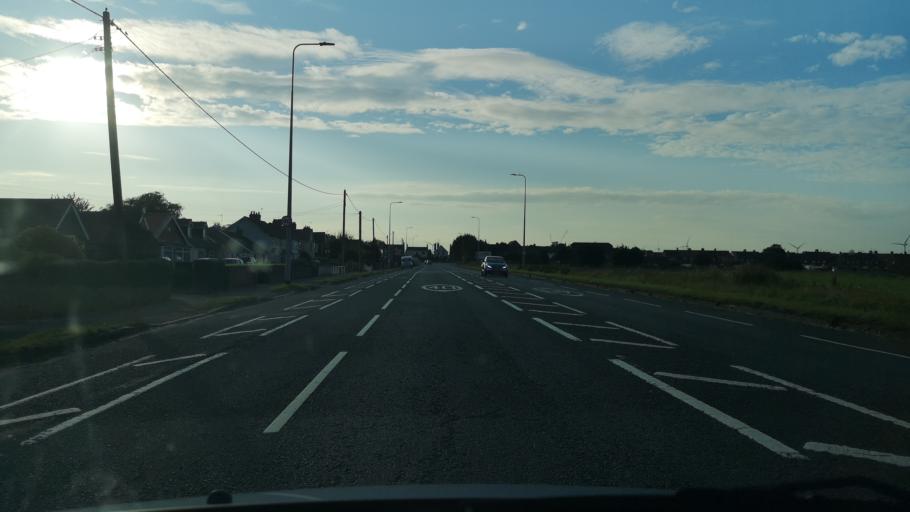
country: GB
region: England
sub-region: North Lincolnshire
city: Gunness
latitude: 53.5906
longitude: -0.7233
